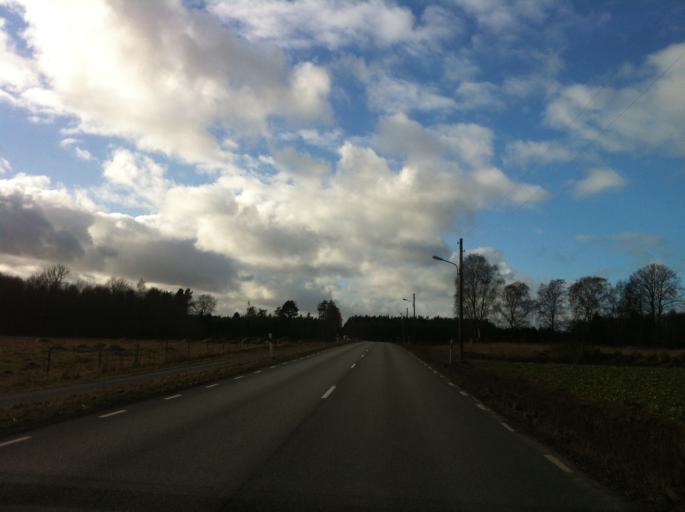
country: SE
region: Skane
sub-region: Bromolla Kommun
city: Bromoella
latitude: 56.0626
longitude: 14.5195
